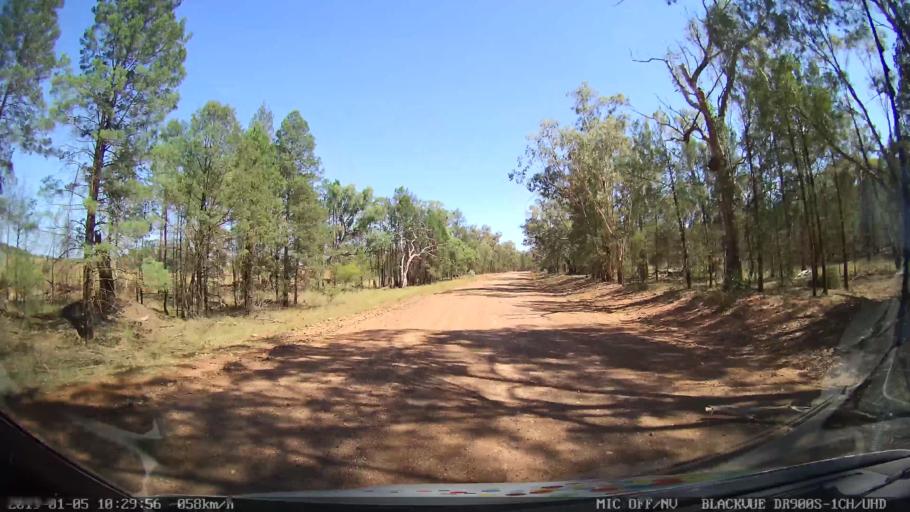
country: AU
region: New South Wales
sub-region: Gilgandra
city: Gilgandra
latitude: -31.5368
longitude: 148.9261
